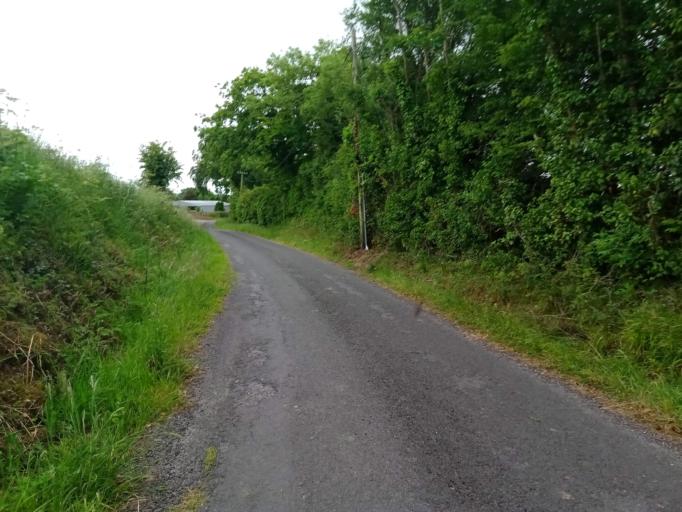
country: IE
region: Leinster
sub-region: Laois
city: Rathdowney
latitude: 52.7745
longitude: -7.4688
